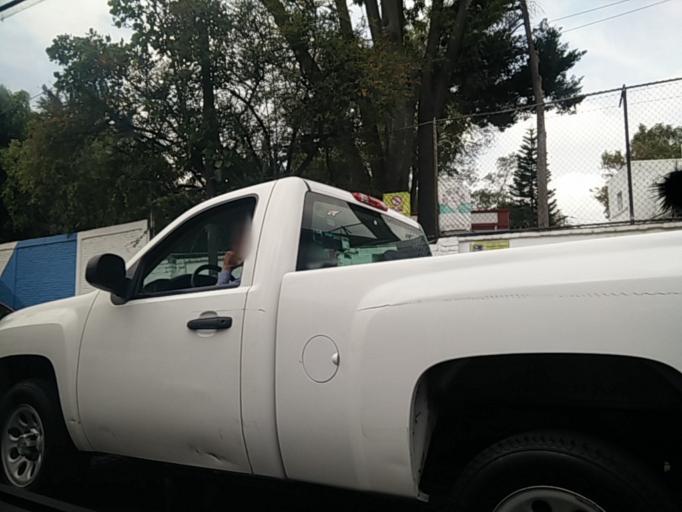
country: MX
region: Mexico City
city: Coyoacan
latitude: 19.3514
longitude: -99.1638
